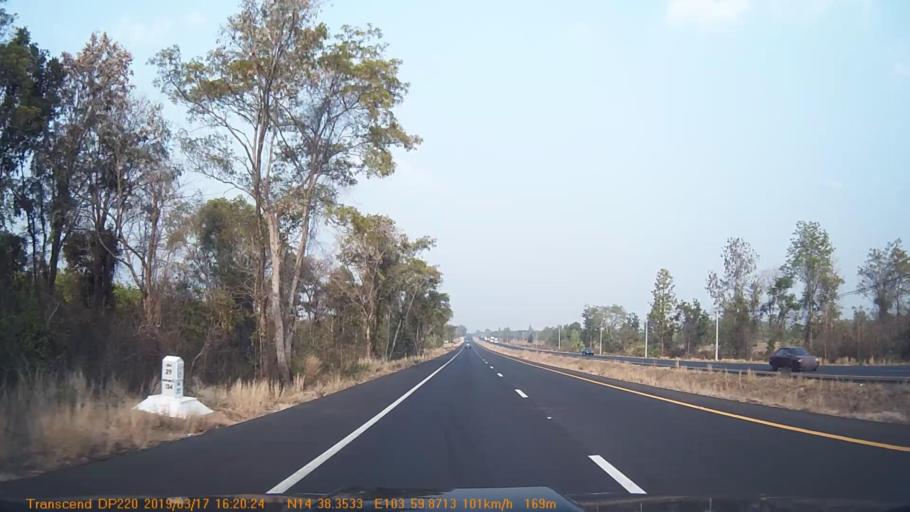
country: TH
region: Surin
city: Bua Chet
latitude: 14.6393
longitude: 103.9981
